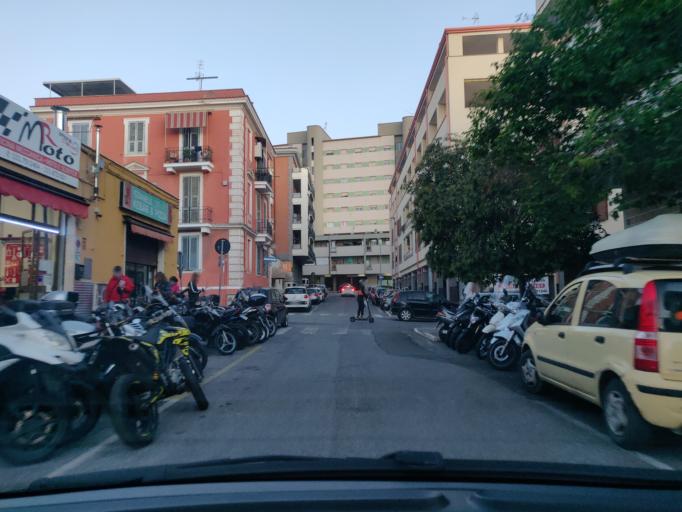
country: IT
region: Latium
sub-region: Citta metropolitana di Roma Capitale
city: Civitavecchia
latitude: 42.0920
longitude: 11.7993
